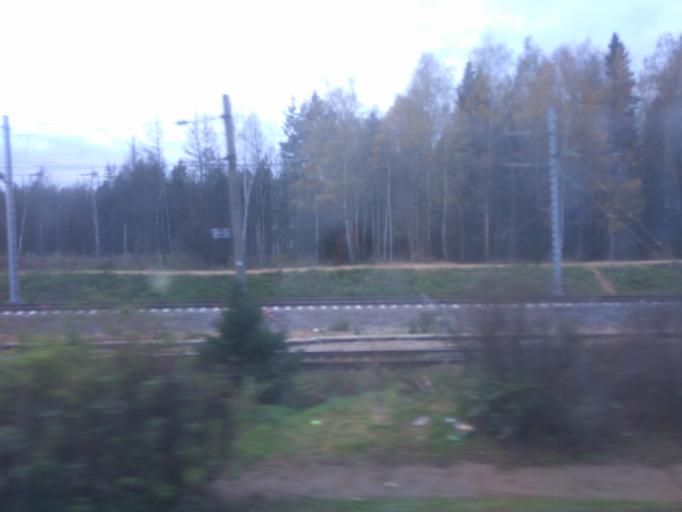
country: RU
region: Moskovskaya
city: Aprelevka
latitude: 55.5633
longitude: 37.0908
